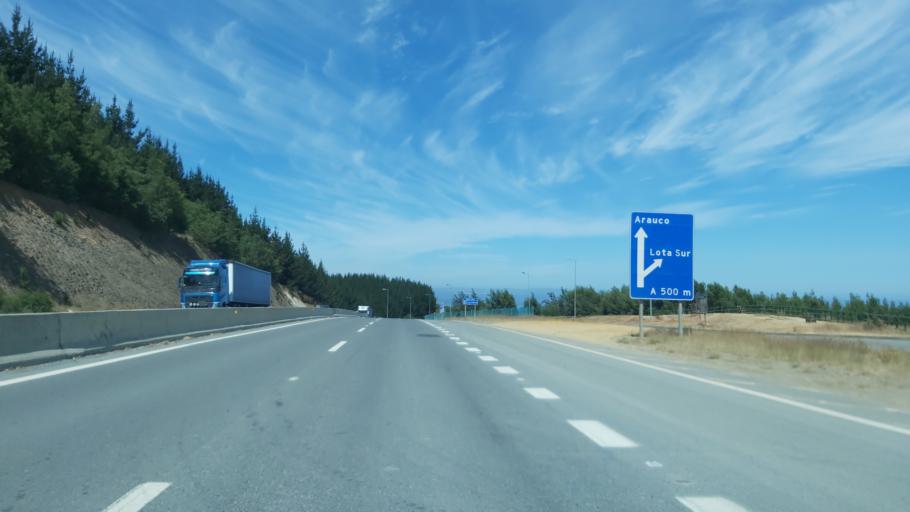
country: CL
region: Biobio
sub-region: Provincia de Concepcion
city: Lota
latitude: -37.0976
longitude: -73.1421
